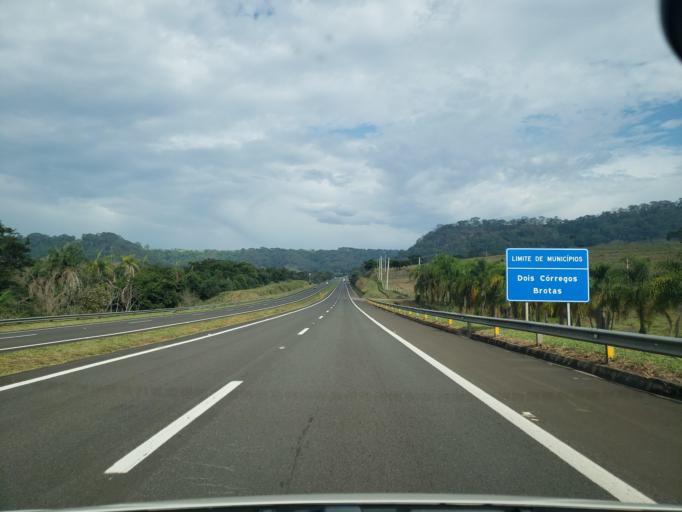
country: BR
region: Sao Paulo
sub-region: Dois Corregos
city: Dois Corregos
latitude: -22.2447
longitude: -48.3261
